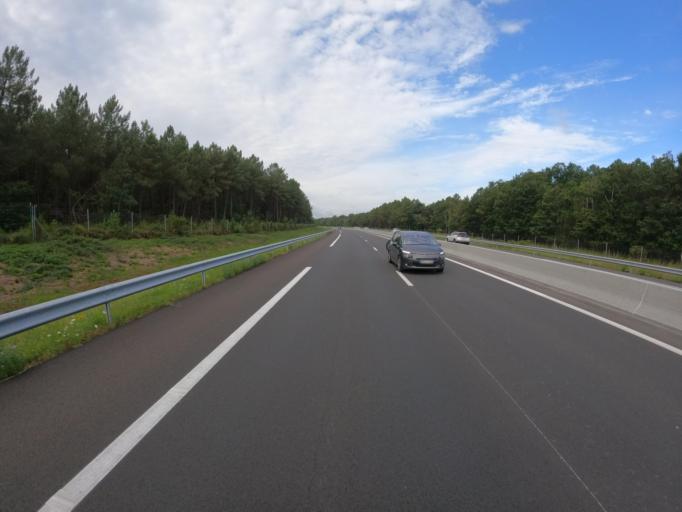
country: FR
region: Centre
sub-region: Departement d'Indre-et-Loire
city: Langeais
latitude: 47.3434
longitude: 0.3582
